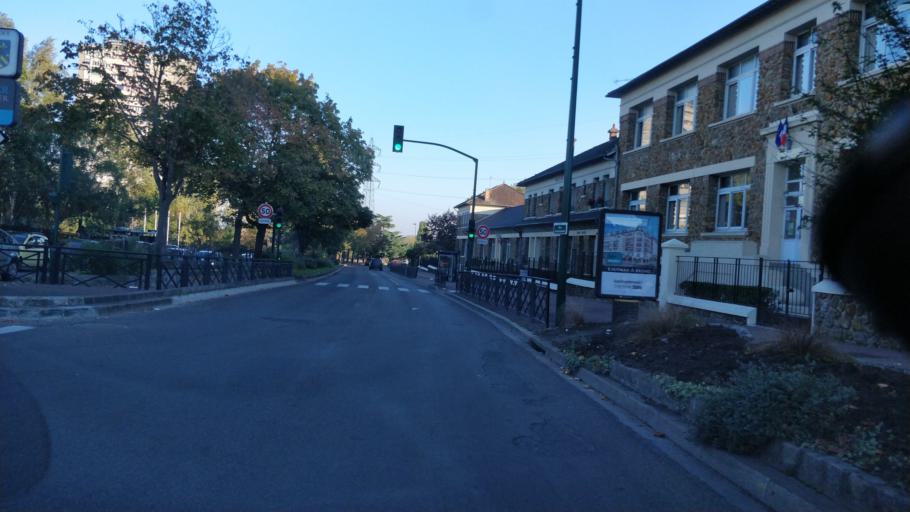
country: FR
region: Ile-de-France
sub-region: Departement de Seine-Saint-Denis
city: Gagny
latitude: 48.8792
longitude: 2.5465
